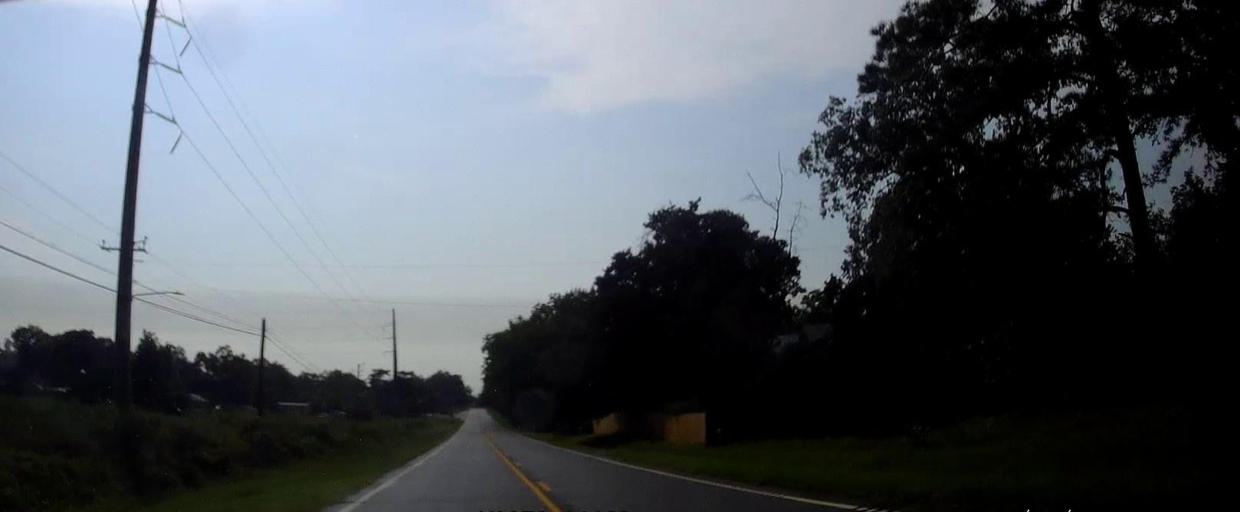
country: US
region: Georgia
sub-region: Twiggs County
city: Jeffersonville
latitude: 32.6024
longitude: -83.2453
